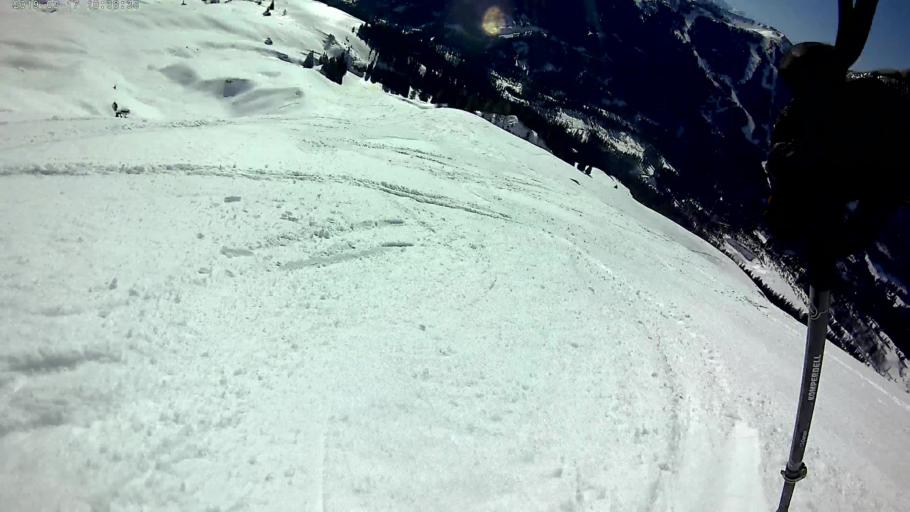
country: AT
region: Salzburg
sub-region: Politischer Bezirk Sankt Johann im Pongau
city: Muhlbach am Hochkonig
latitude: 47.4070
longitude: 13.0812
